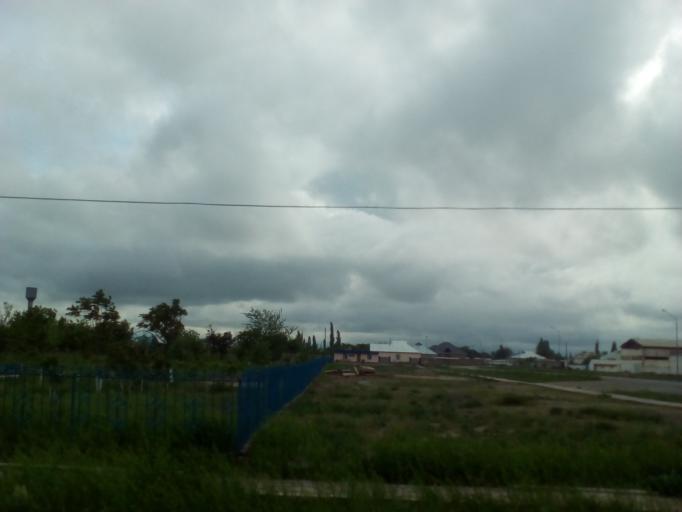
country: KZ
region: Ongtustik Qazaqstan
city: Sholaqqkorghan
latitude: 43.7573
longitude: 69.1900
